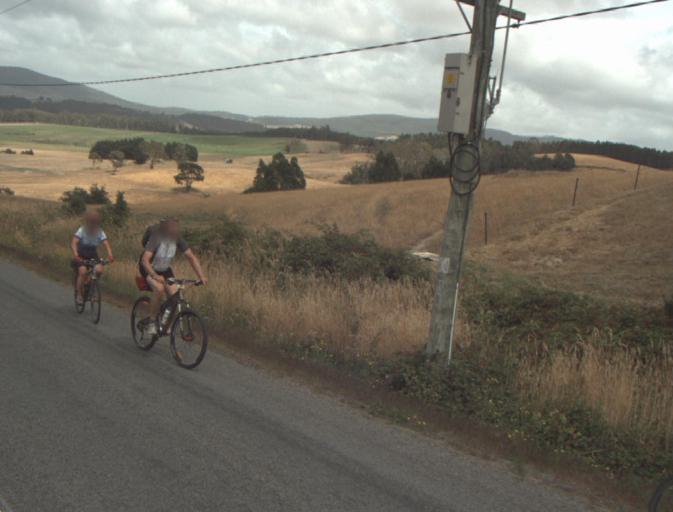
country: AU
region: Tasmania
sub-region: Launceston
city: Mayfield
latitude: -41.2209
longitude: 147.2066
